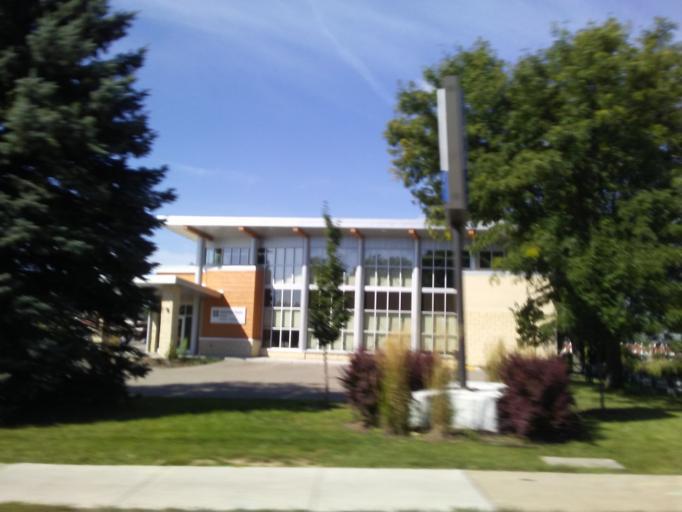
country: US
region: Wisconsin
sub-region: Dane County
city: Madison
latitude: 43.0512
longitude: -89.3946
